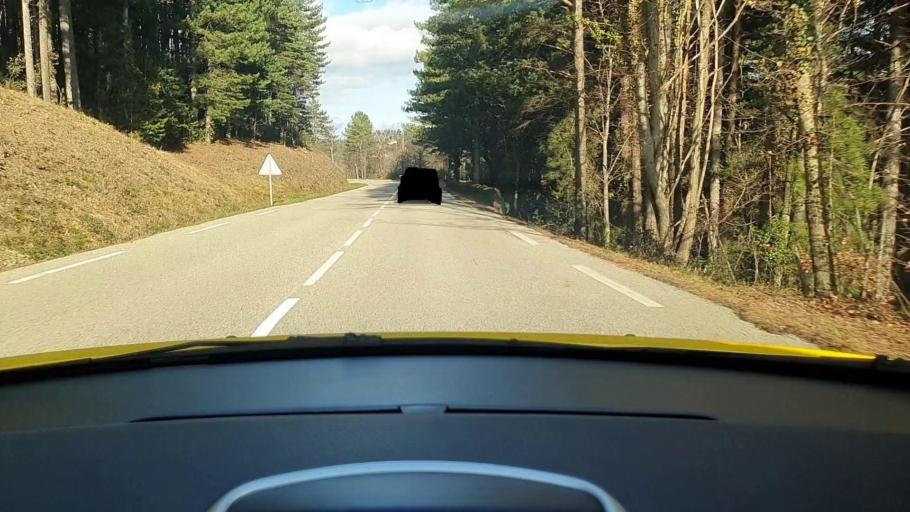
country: FR
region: Languedoc-Roussillon
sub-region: Departement du Gard
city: Branoux-les-Taillades
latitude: 44.3567
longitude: 3.9558
